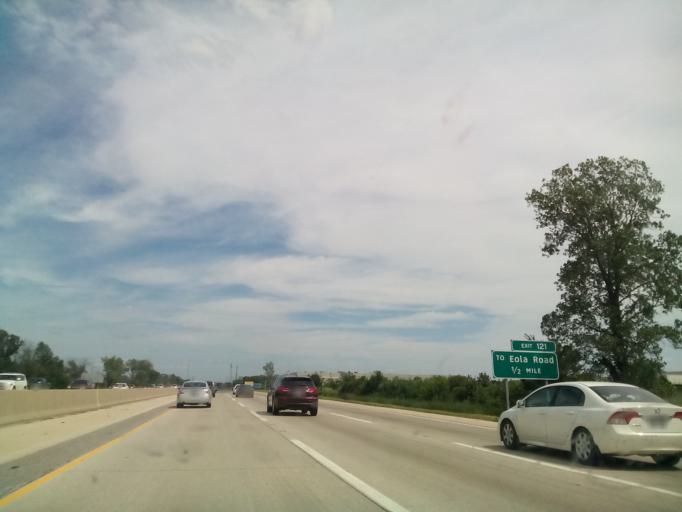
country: US
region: Illinois
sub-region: Kane County
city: North Aurora
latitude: 41.7994
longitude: -88.2651
